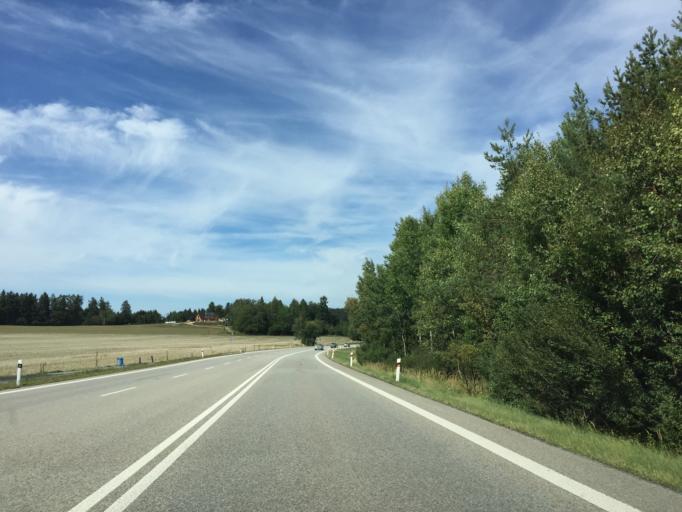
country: CZ
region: Central Bohemia
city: Votice
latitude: 49.6079
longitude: 14.6599
